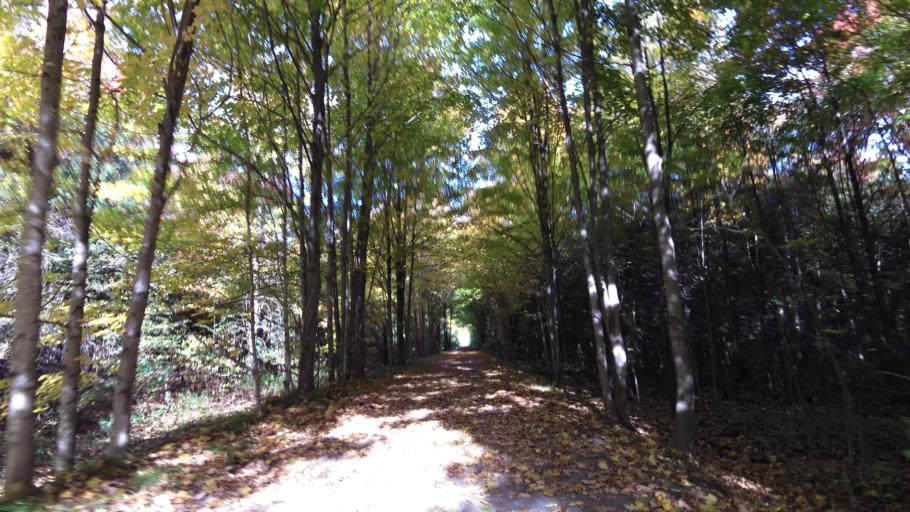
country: CA
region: Ontario
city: Orangeville
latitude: 43.7850
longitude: -80.0576
